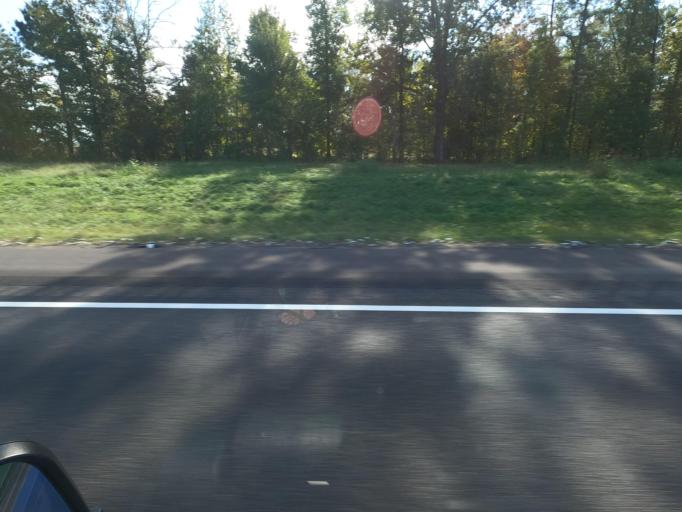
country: US
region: Tennessee
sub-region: Fayette County
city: Hickory Withe
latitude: 35.3058
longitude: -89.5906
